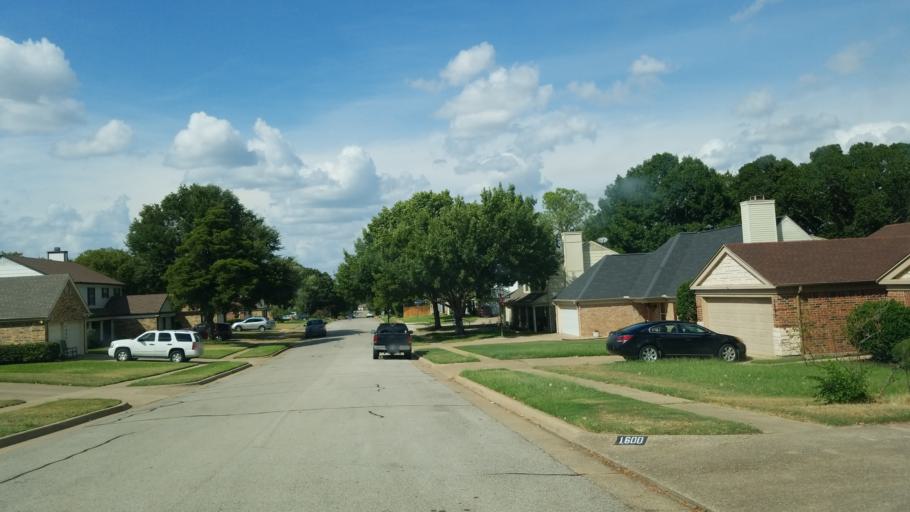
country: US
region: Texas
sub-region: Tarrant County
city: Euless
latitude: 32.8592
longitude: -97.0777
